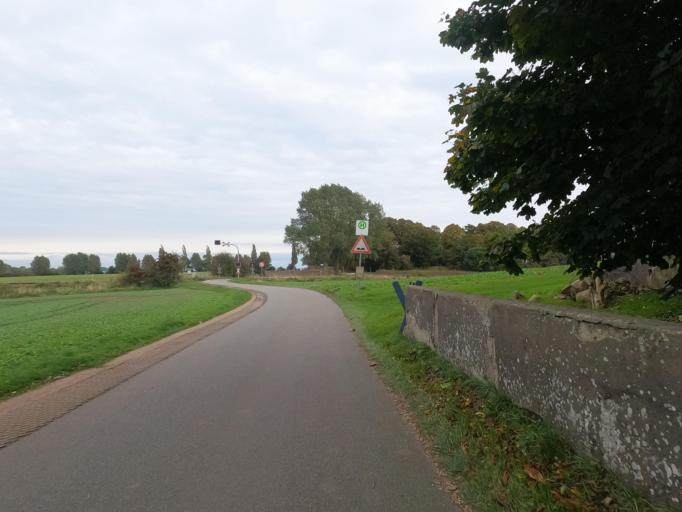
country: DE
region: Schleswig-Holstein
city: Neukirchen
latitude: 54.3462
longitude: 11.0442
